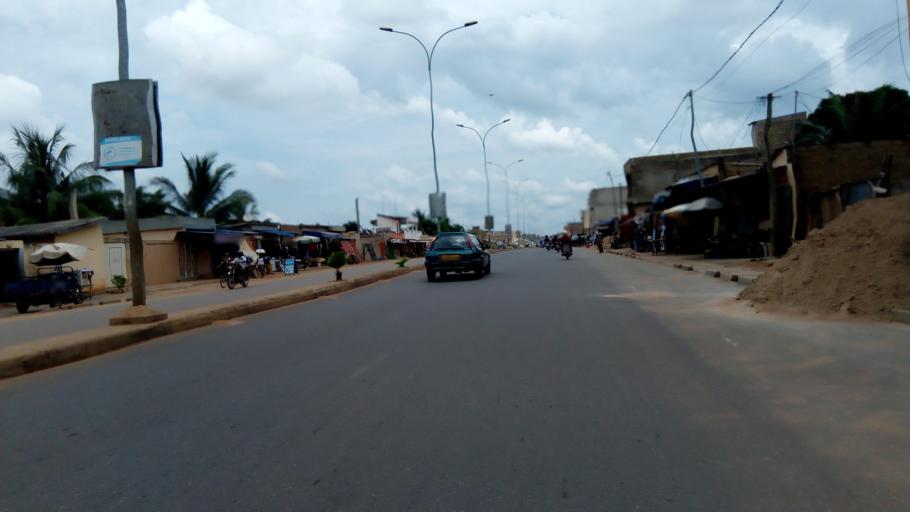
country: TG
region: Maritime
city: Lome
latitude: 6.2142
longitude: 1.1741
